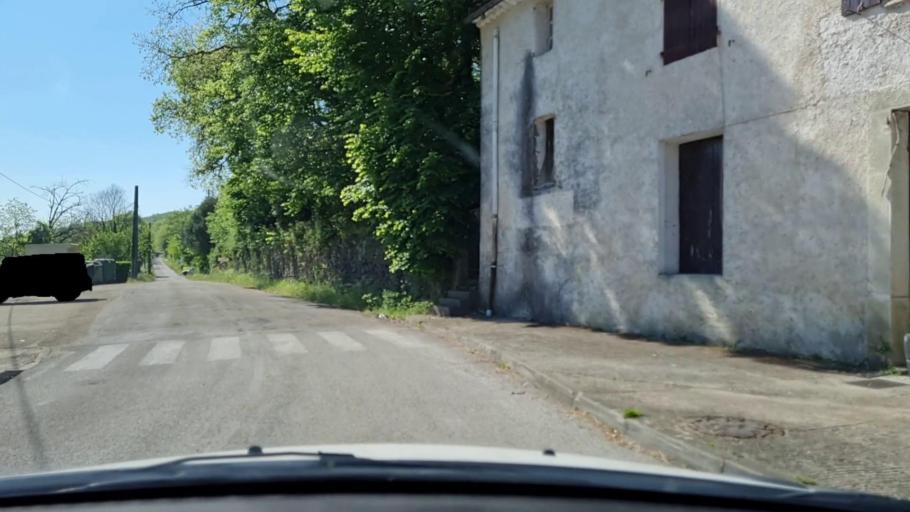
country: FR
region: Languedoc-Roussillon
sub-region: Departement du Gard
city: Cendras
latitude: 44.1543
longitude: 4.0381
